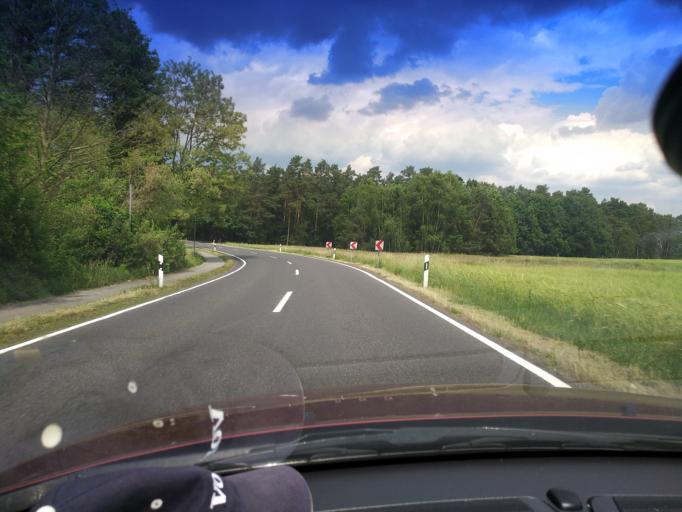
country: DE
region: Saxony
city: Mucka
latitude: 51.3252
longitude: 14.7026
